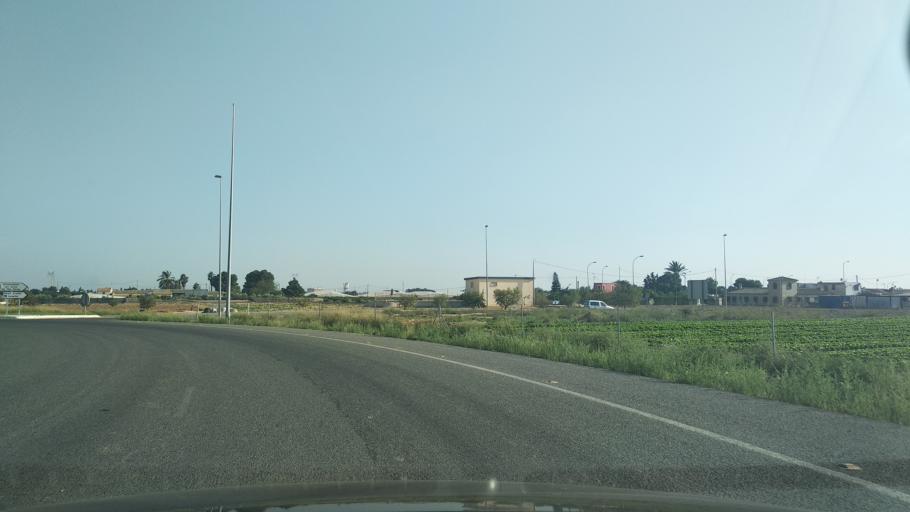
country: ES
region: Murcia
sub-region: Murcia
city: San Javier
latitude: 37.8211
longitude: -0.8499
